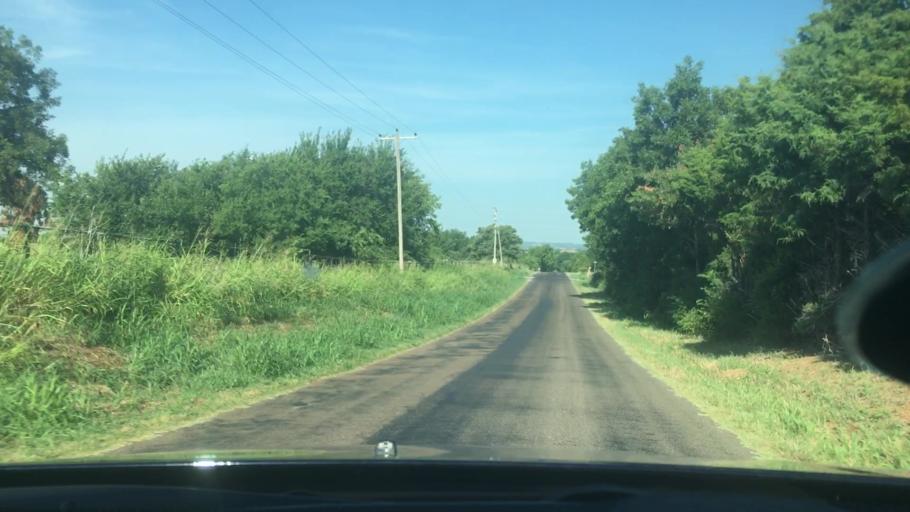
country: US
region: Oklahoma
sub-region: Garvin County
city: Maysville
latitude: 34.6521
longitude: -97.3860
